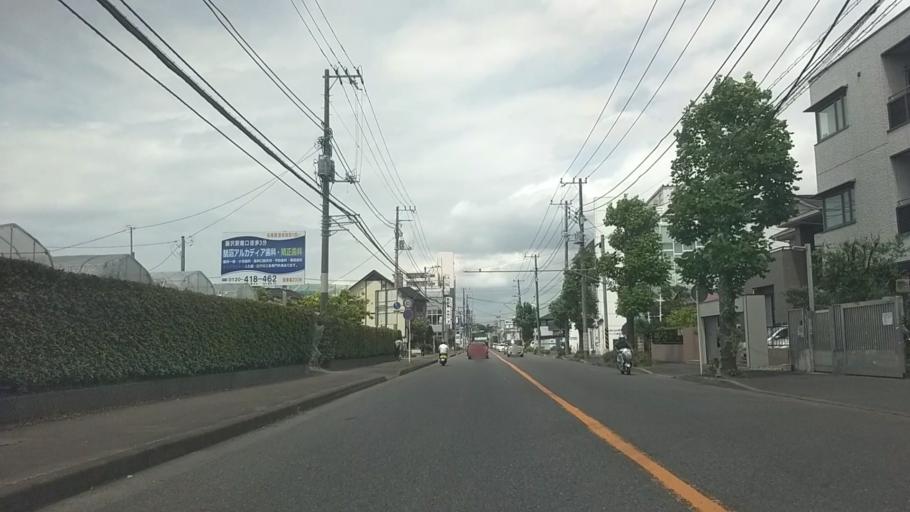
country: JP
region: Kanagawa
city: Fujisawa
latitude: 35.3313
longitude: 139.5077
